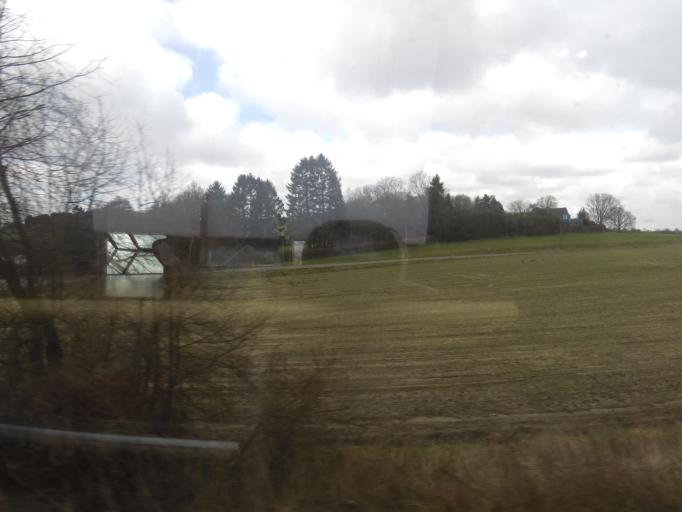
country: DE
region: Lower Saxony
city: Seevetal
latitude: 53.4103
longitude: 10.0136
